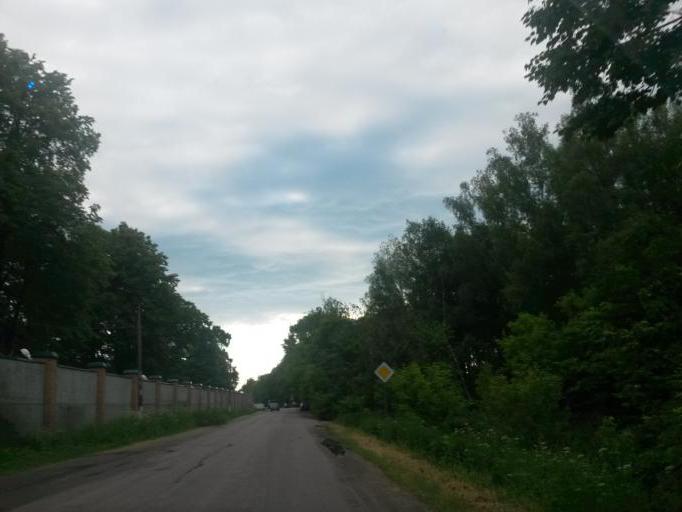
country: RU
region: Moskovskaya
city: Lyubuchany
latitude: 55.2493
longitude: 37.6328
